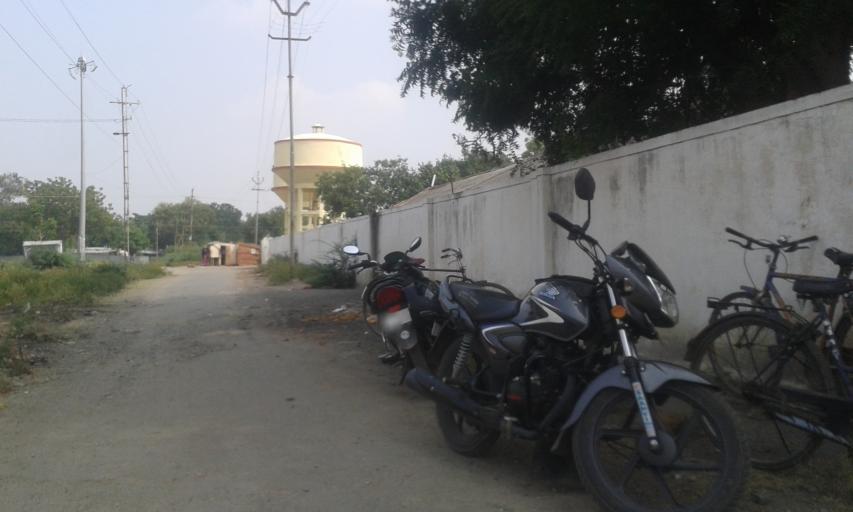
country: IN
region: Karnataka
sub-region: Raichur
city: Lingsugur
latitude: 16.1914
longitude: 76.6601
